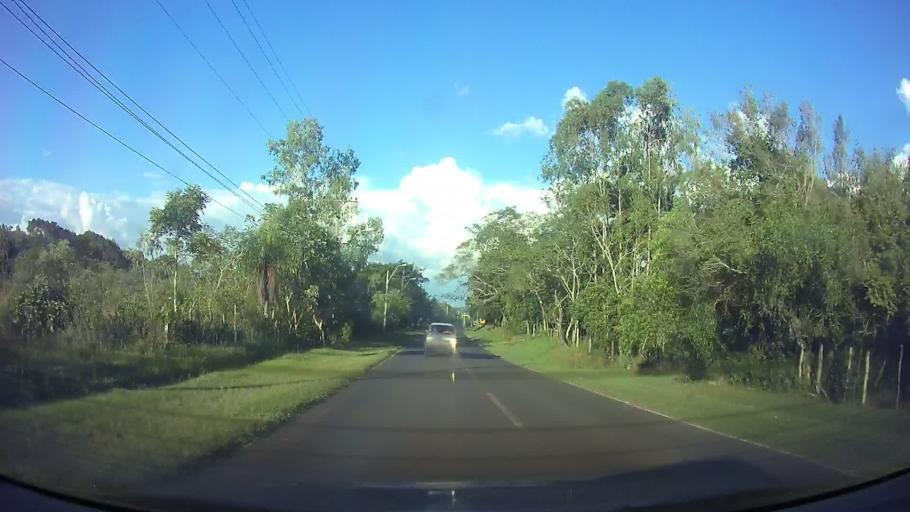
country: PY
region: Cordillera
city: Emboscada
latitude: -25.1946
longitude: -57.3164
